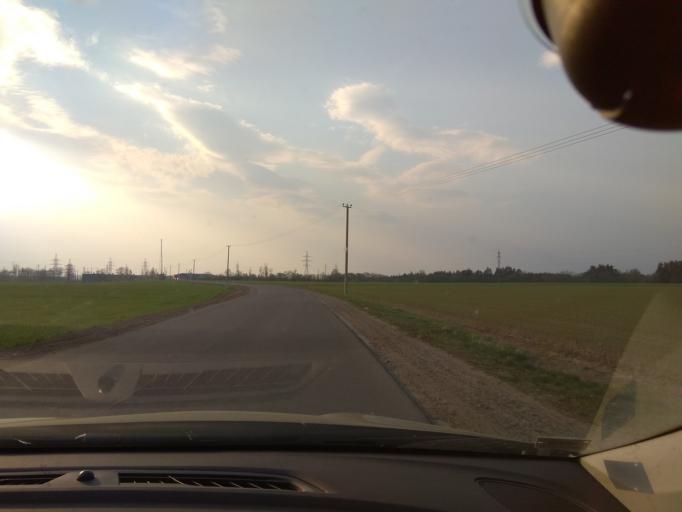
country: LT
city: Baltoji Voke
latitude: 54.6091
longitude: 25.1283
